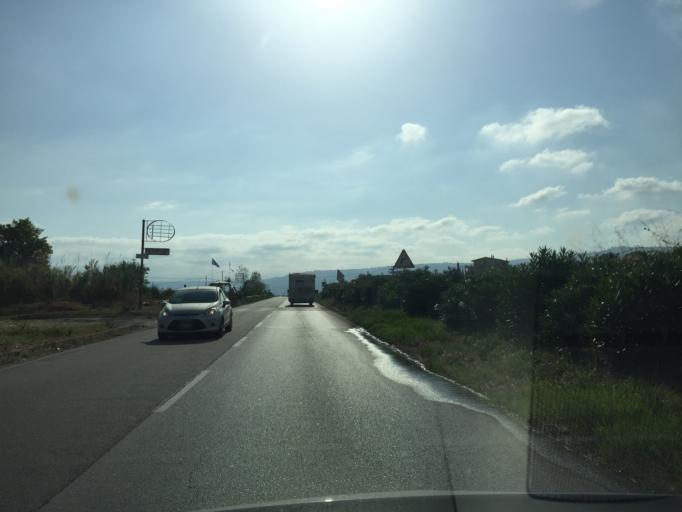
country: IT
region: Calabria
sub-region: Provincia di Vibo-Valentia
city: Pannaconi
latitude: 38.7158
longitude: 16.0582
